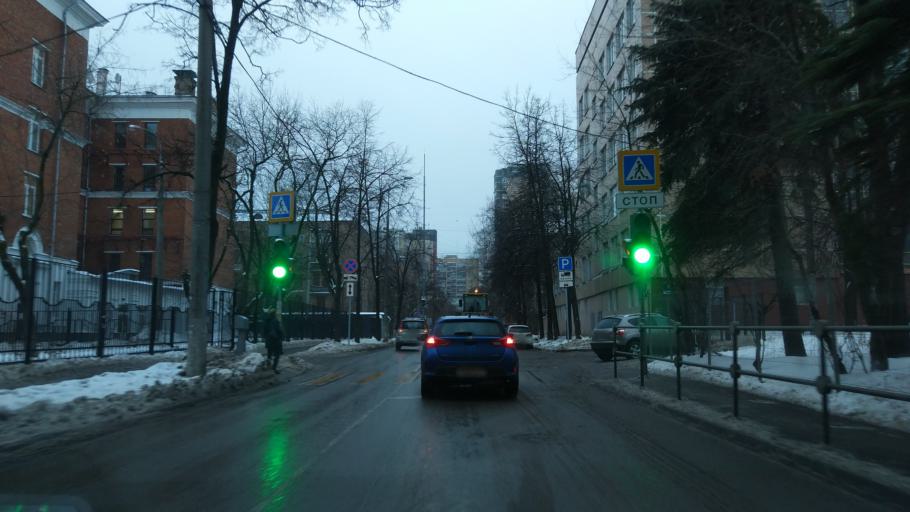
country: RU
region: Moskovskaya
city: Izmaylovo
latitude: 55.7910
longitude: 37.7972
